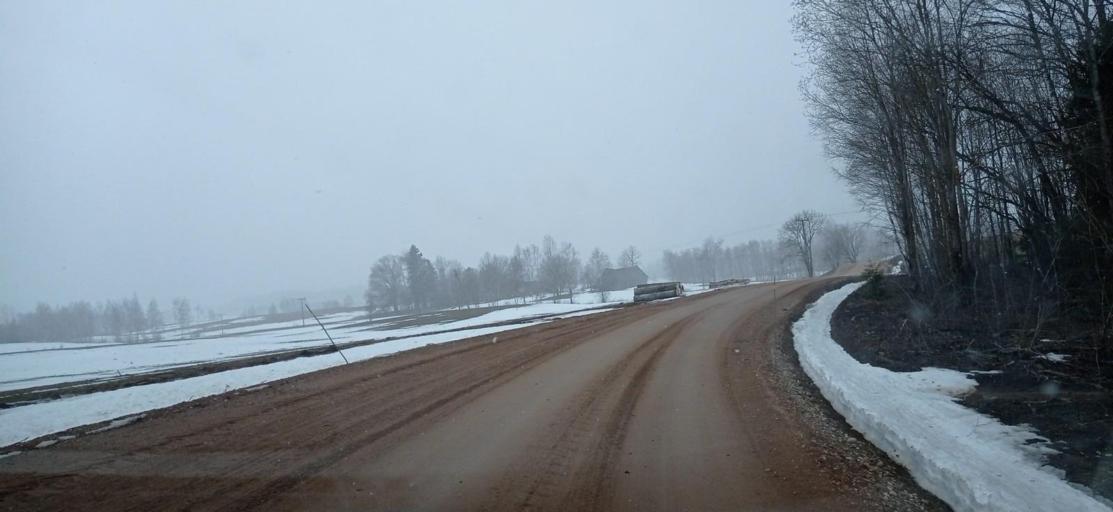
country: EE
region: Tartu
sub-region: UElenurme vald
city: Ulenurme
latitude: 58.1112
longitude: 26.6951
